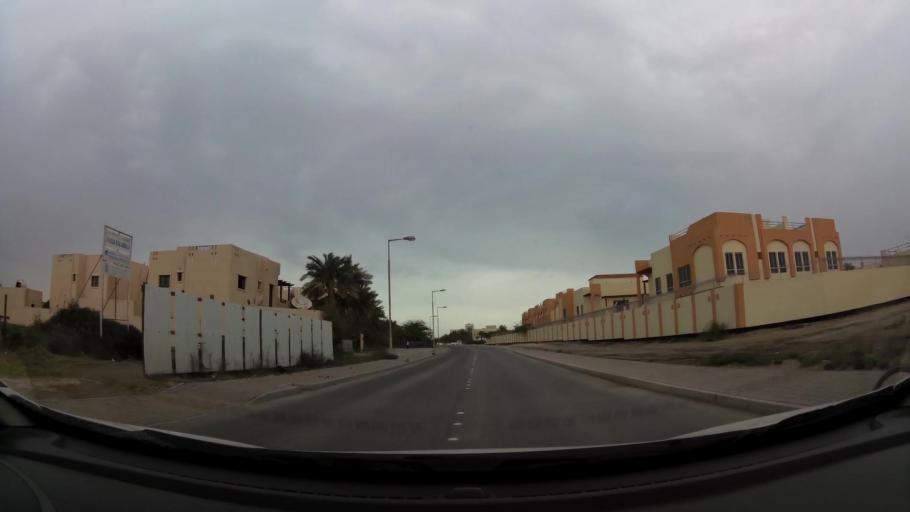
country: BH
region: Central Governorate
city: Madinat Hamad
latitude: 26.1470
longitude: 50.4562
